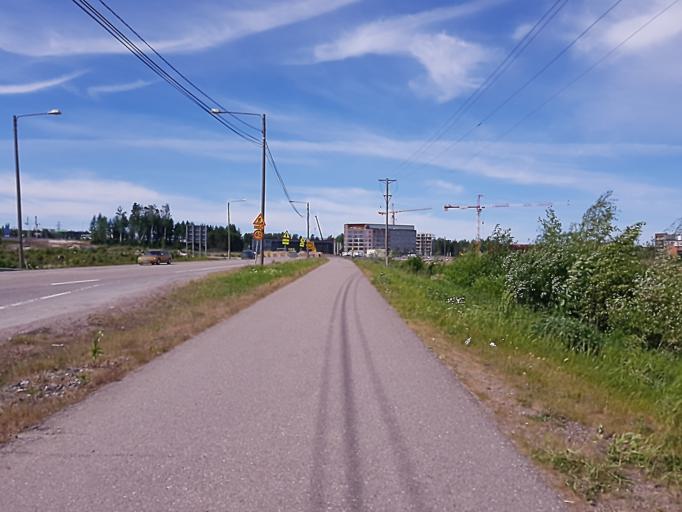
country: FI
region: Uusimaa
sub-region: Helsinki
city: Kilo
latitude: 60.3117
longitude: 24.8476
